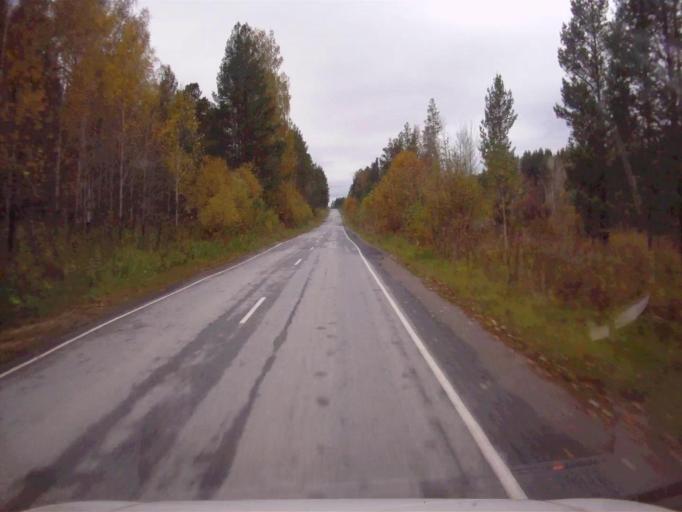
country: RU
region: Chelyabinsk
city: Nyazepetrovsk
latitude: 56.0529
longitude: 59.4819
